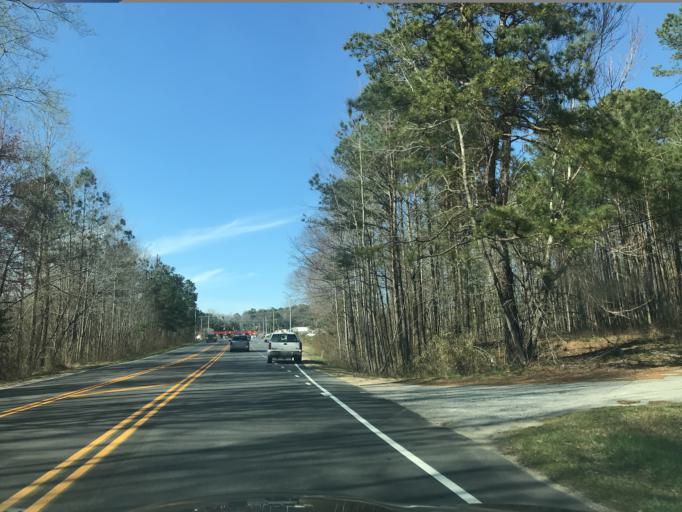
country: US
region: North Carolina
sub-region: Wake County
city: Fuquay-Varina
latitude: 35.5939
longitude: -78.7585
